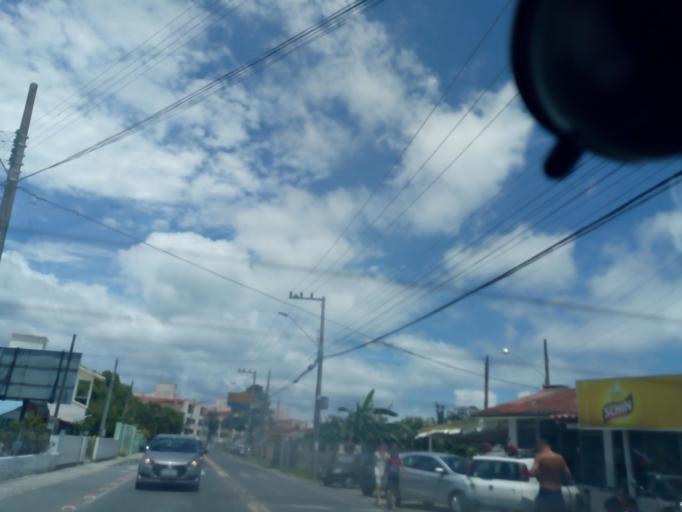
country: BR
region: Santa Catarina
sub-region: Florianopolis
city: Itacorubi
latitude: -27.3972
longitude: -48.4278
